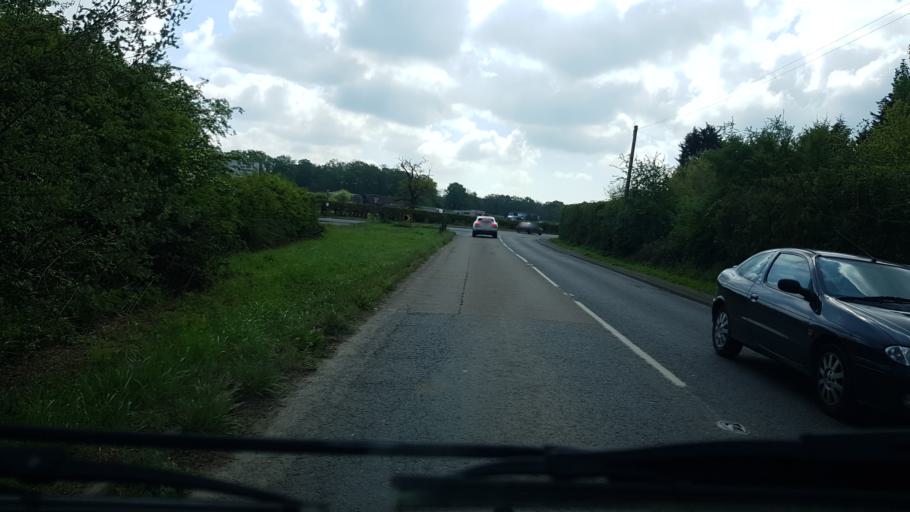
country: GB
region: England
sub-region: Surrey
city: Leatherhead
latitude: 51.3102
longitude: -0.3510
